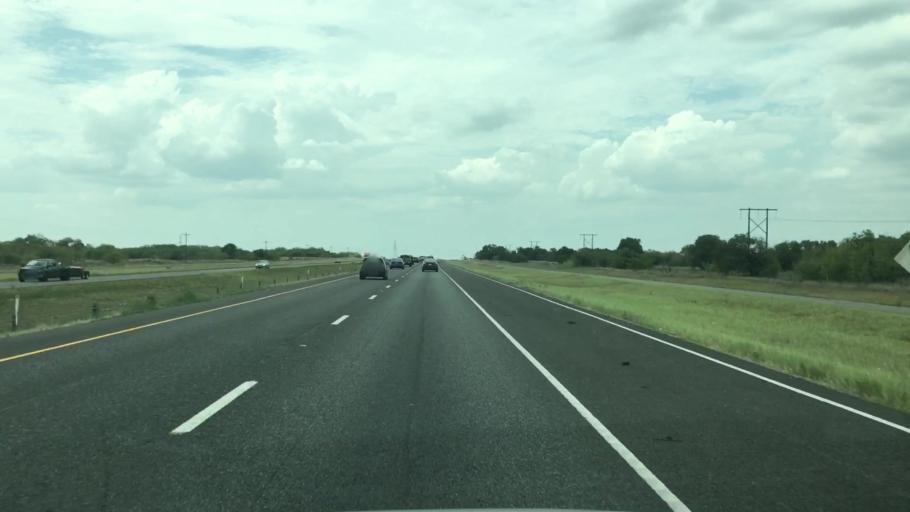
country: US
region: Texas
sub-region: Atascosa County
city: Pleasanton
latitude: 28.8107
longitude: -98.3516
